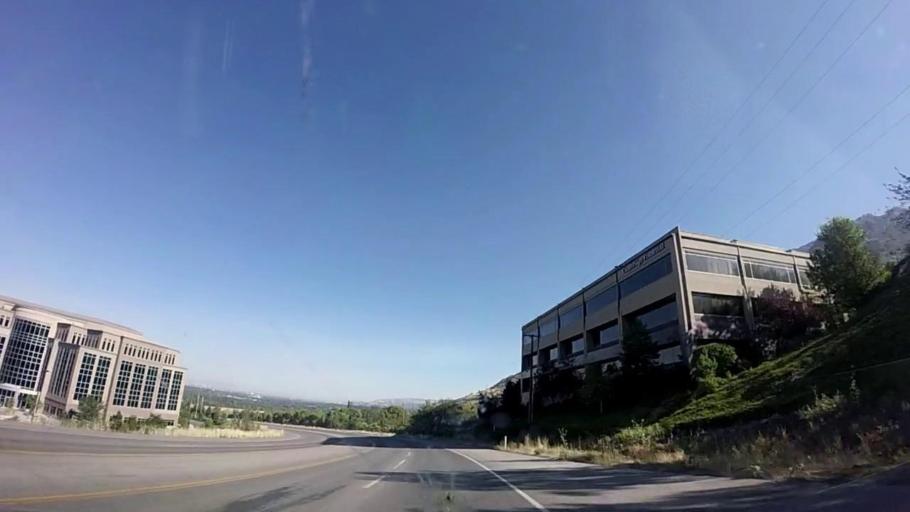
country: US
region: Utah
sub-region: Salt Lake County
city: Cottonwood Heights
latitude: 40.6333
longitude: -111.8000
